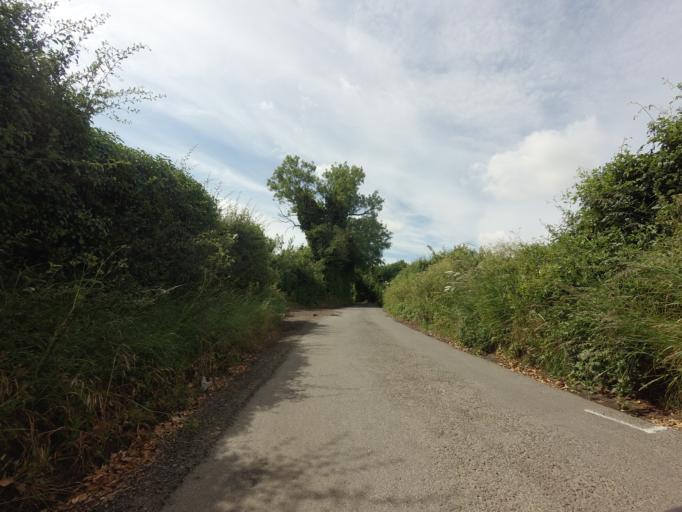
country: GB
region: England
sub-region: Kent
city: Halstead
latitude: 51.3607
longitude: 0.1313
